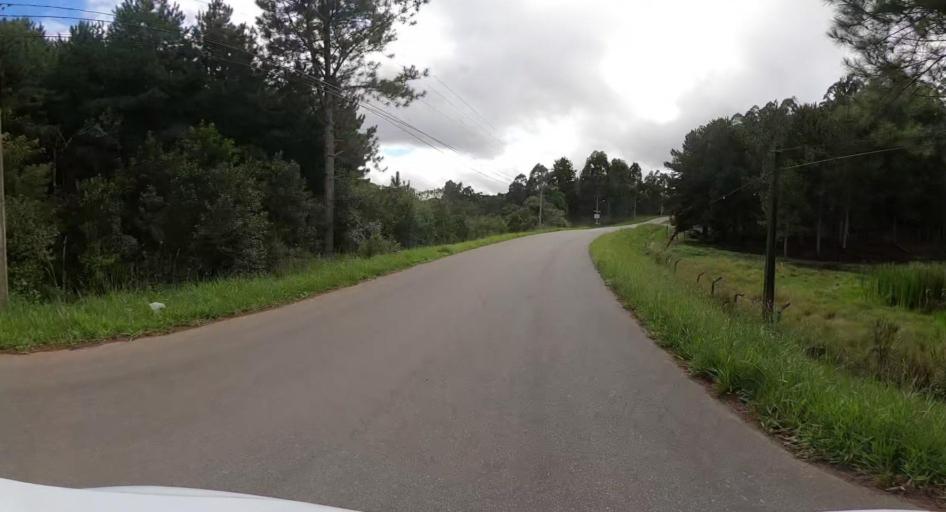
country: BR
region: Parana
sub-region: Campina Grande Do Sul
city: Campina Grande do Sul
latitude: -25.2986
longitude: -49.0420
